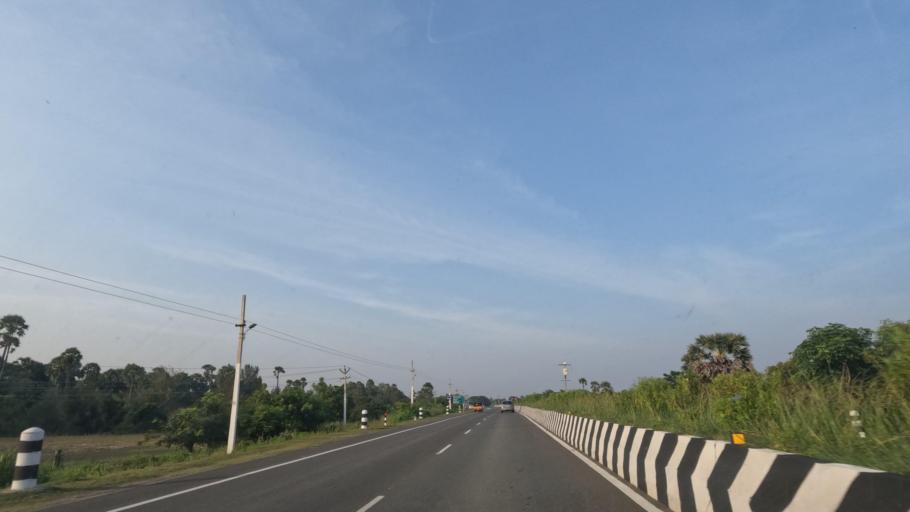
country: IN
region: Tamil Nadu
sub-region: Kancheepuram
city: Mamallapuram
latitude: 12.6801
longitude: 80.2138
